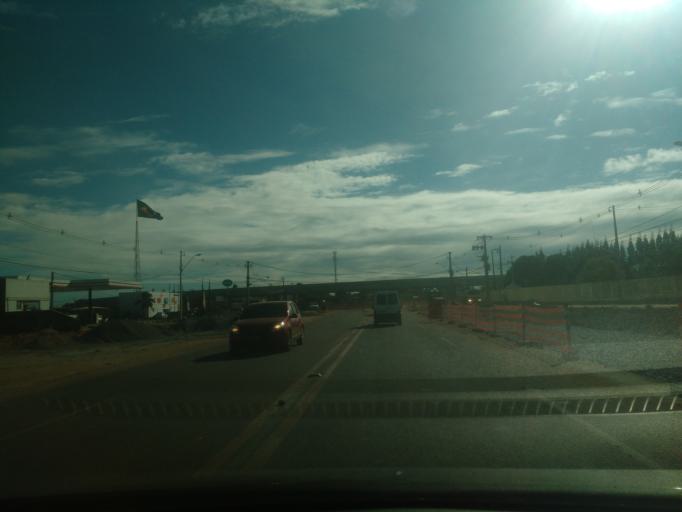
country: BR
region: Alagoas
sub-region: Satuba
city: Satuba
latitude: -9.5649
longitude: -35.7755
